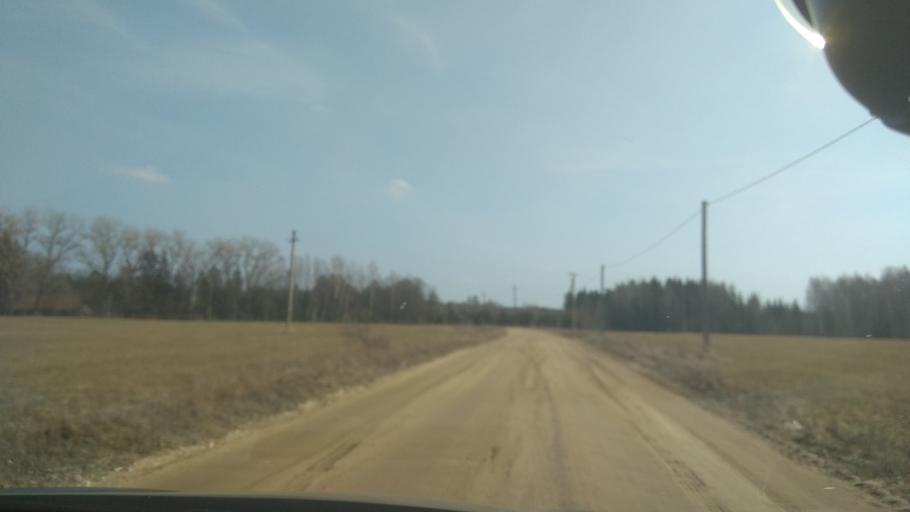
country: LT
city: Baltoji Voke
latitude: 54.4829
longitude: 25.2650
